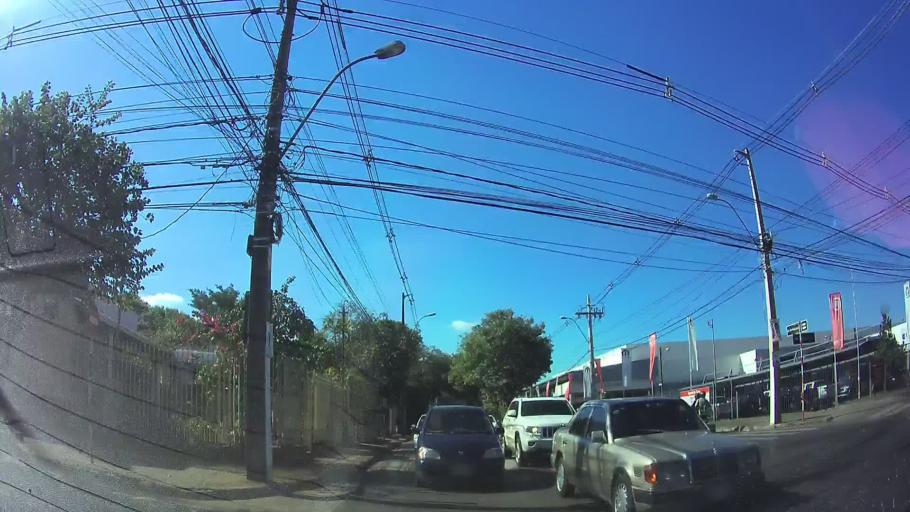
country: PY
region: Central
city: Lambare
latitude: -25.3155
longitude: -57.5733
